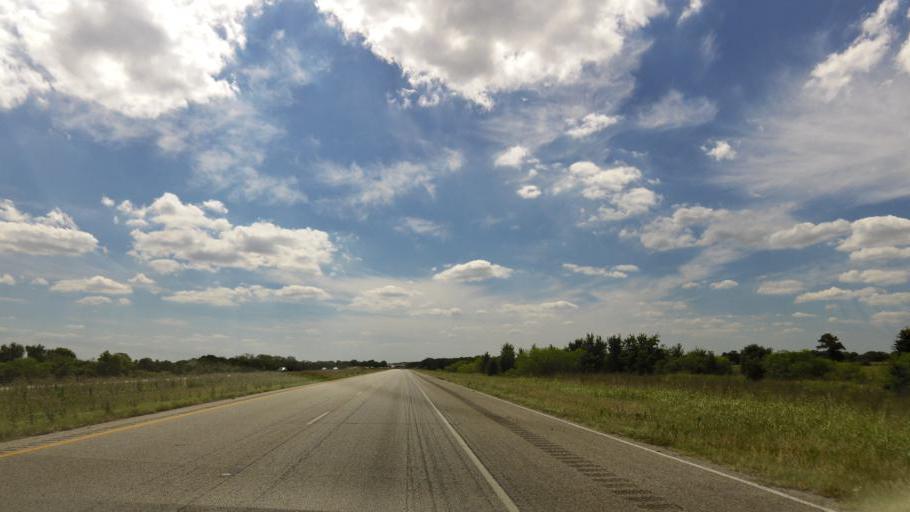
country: US
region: Texas
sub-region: Gonzales County
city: Waelder
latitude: 29.6642
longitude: -97.3657
